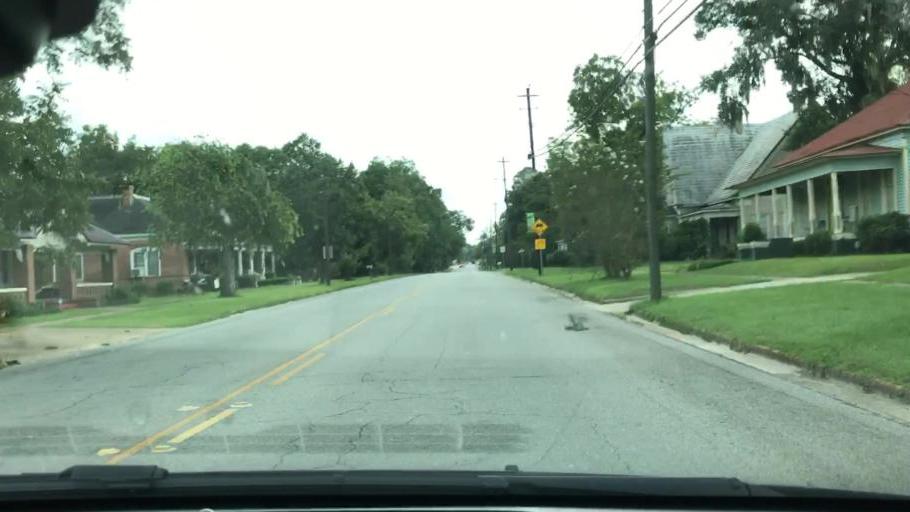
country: US
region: Georgia
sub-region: Clay County
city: Fort Gaines
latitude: 31.6110
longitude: -85.0498
